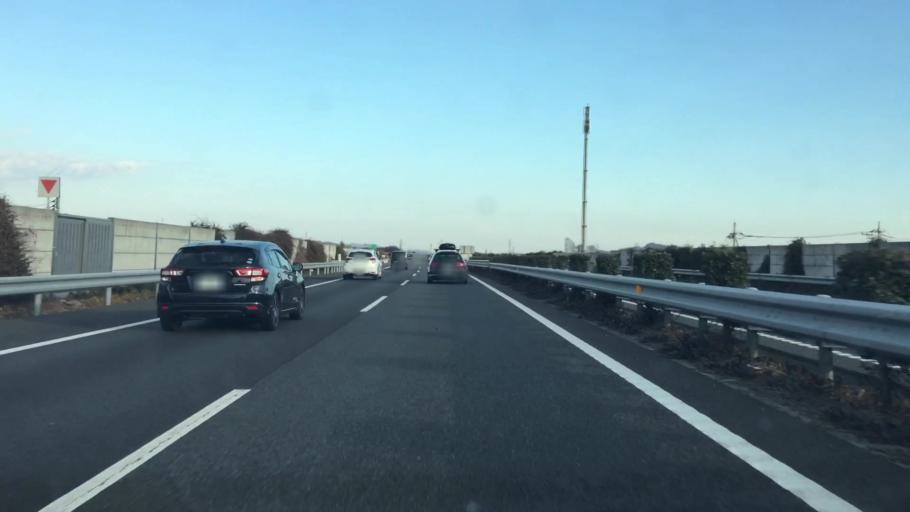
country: JP
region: Gunma
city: Kiryu
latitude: 36.3459
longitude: 139.2868
